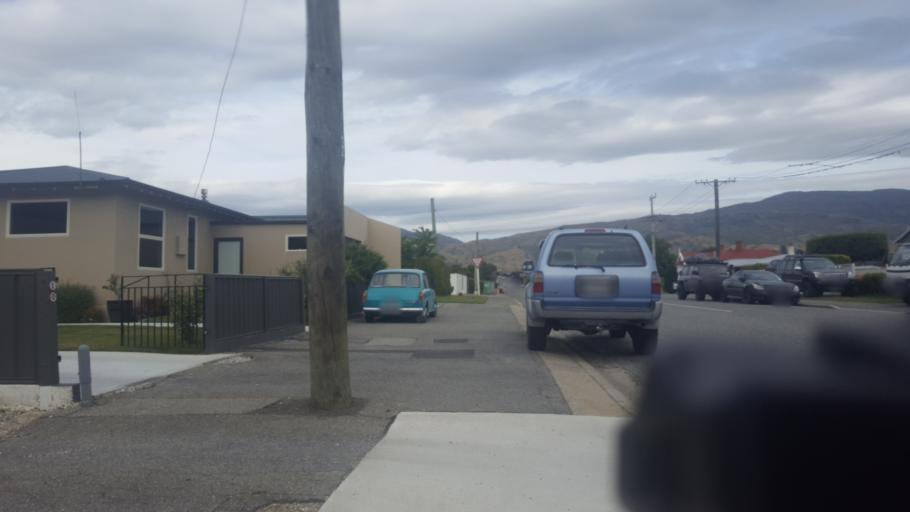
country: NZ
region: Otago
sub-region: Queenstown-Lakes District
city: Wanaka
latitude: -45.0457
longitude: 169.2115
